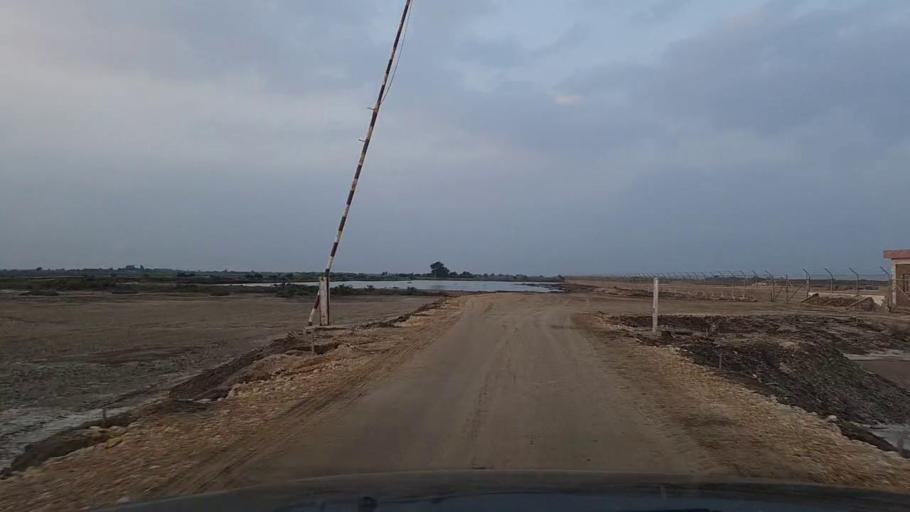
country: PK
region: Sindh
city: Jati
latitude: 24.4938
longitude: 68.3918
